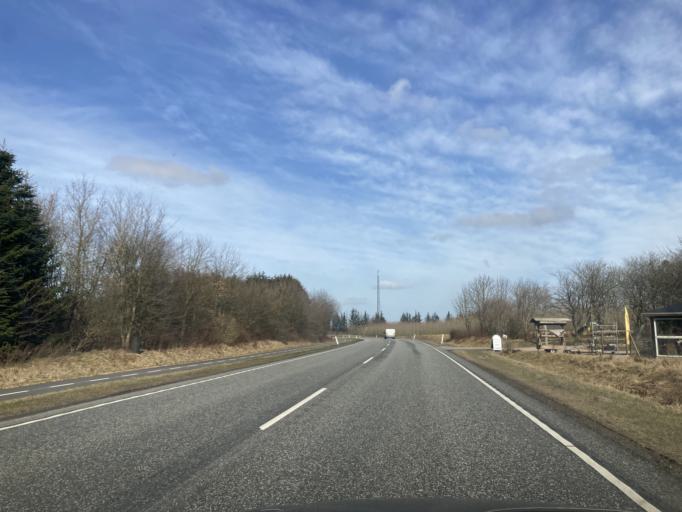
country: DK
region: Central Jutland
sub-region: Hedensted Kommune
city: Torring
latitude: 55.9828
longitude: 9.3931
